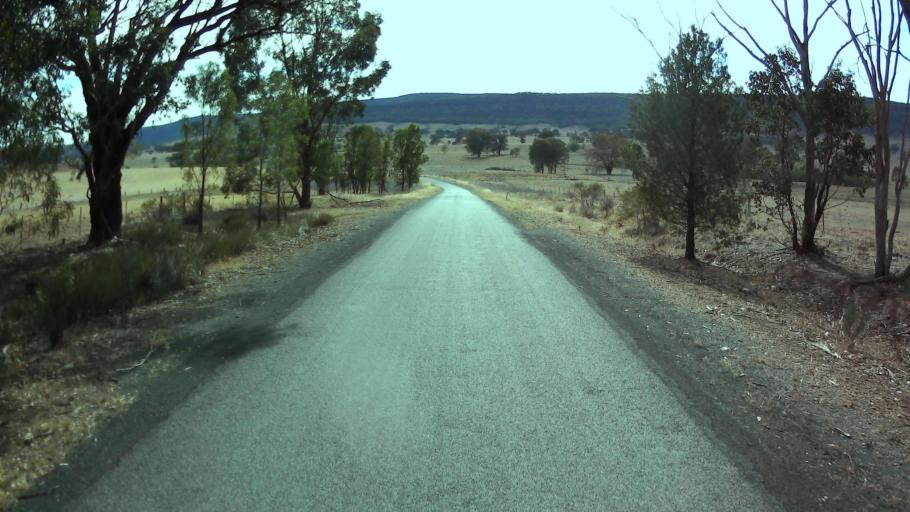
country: AU
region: New South Wales
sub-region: Weddin
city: Grenfell
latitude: -33.8283
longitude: 148.2810
